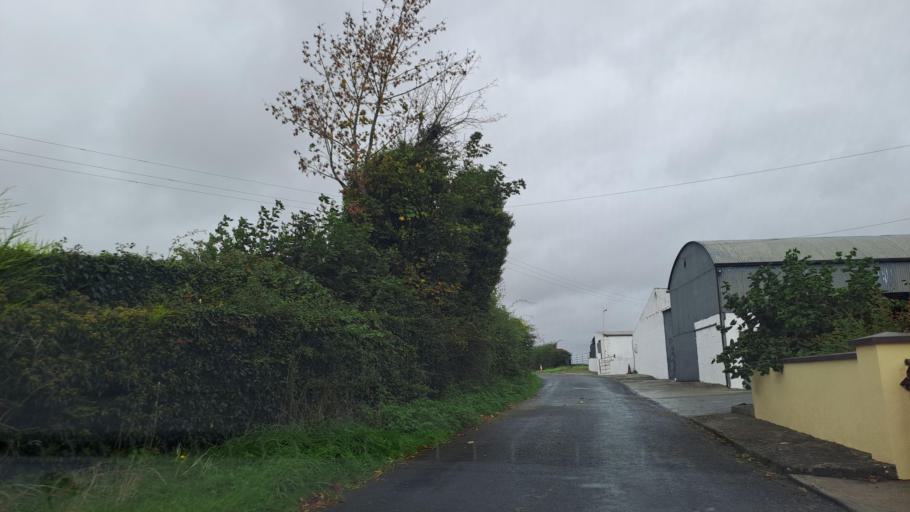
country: IE
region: Ulster
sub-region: County Monaghan
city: Carrickmacross
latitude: 53.9648
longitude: -6.7578
